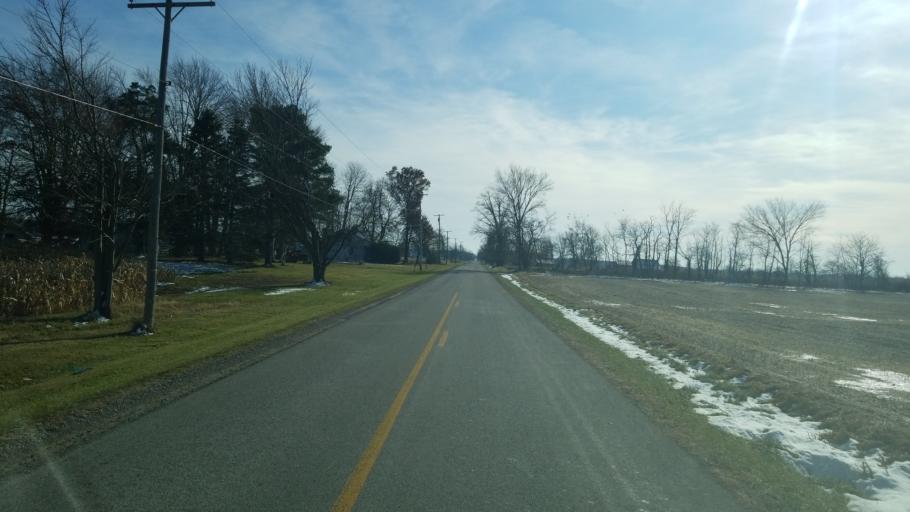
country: US
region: Ohio
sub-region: Huron County
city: New London
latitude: 41.1352
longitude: -82.3491
